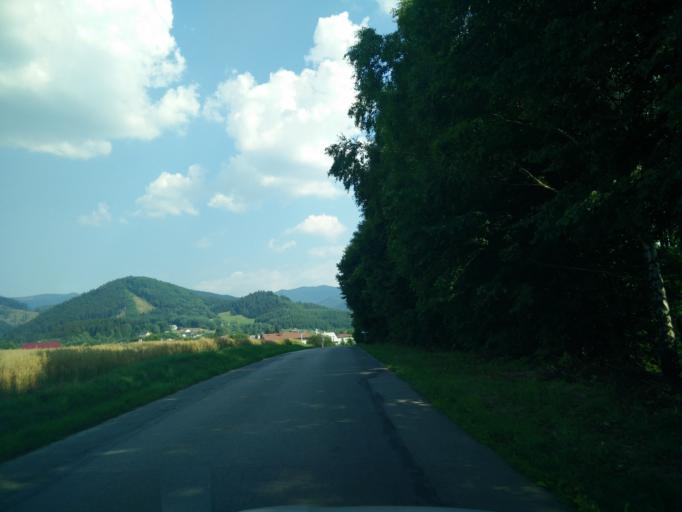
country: SK
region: Zilinsky
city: Rajec
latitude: 49.1036
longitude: 18.7010
